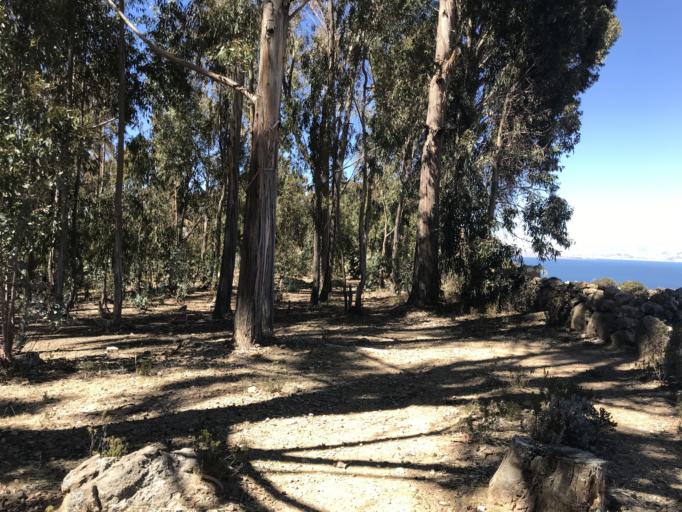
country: BO
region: La Paz
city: Yumani
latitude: -16.0386
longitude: -69.1492
